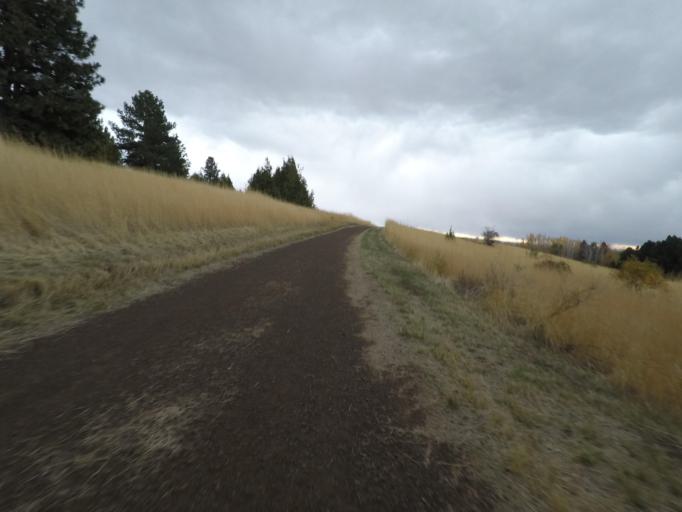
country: US
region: Washington
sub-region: Walla Walla County
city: Walla Walla East
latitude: 46.0702
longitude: -118.2567
